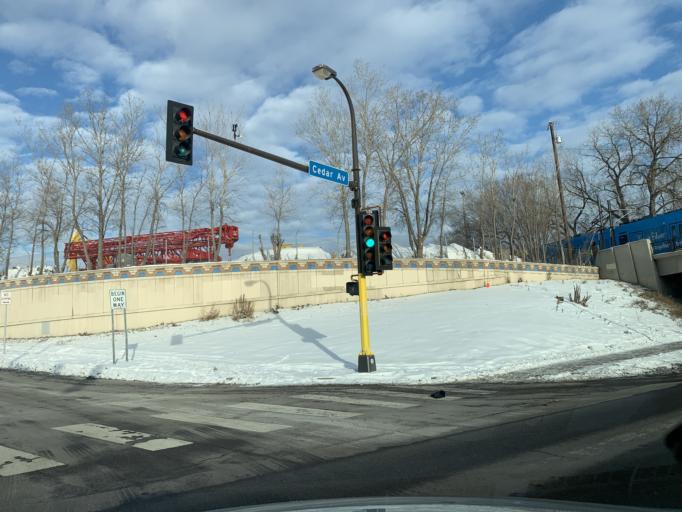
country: US
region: Minnesota
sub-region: Hennepin County
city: Minneapolis
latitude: 44.9606
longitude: -93.2462
